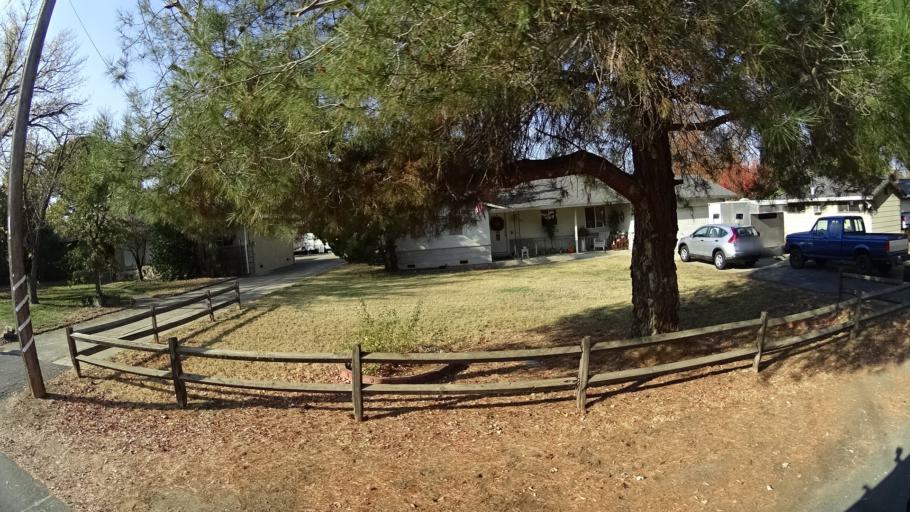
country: US
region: California
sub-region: Sacramento County
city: Citrus Heights
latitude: 38.7092
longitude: -121.2680
